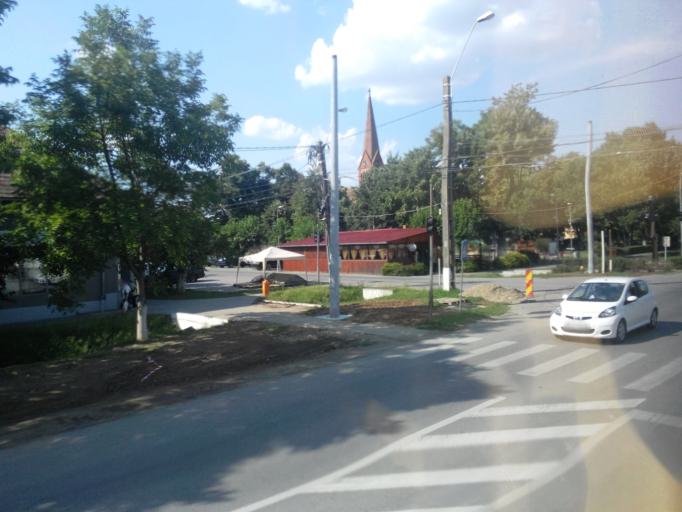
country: RO
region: Timis
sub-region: Comuna Dumbravita
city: Dumbravita
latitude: 45.8009
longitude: 21.2477
